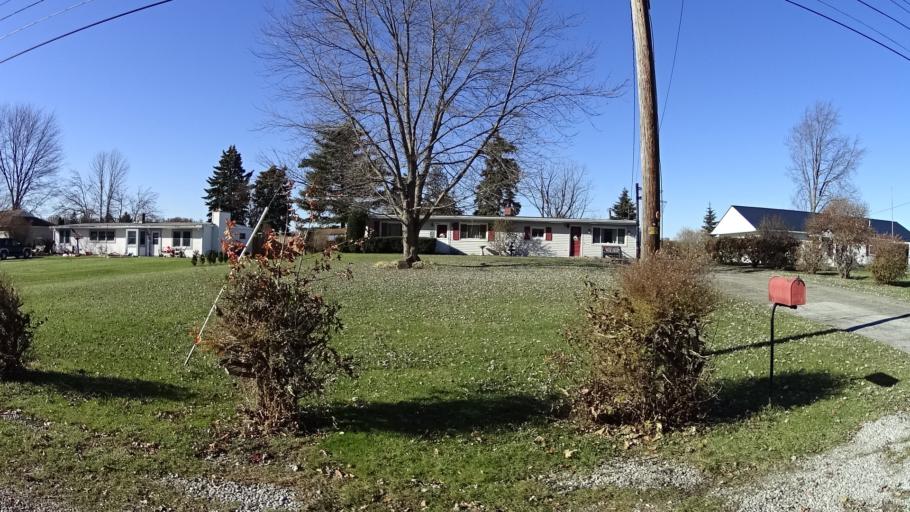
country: US
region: Ohio
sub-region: Lorain County
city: Elyria
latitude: 41.3613
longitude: -82.0681
